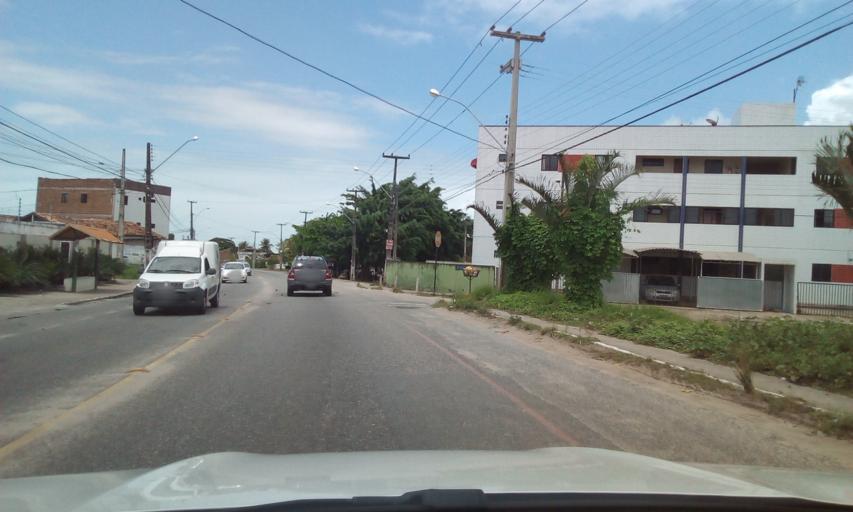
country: BR
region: Paraiba
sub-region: Joao Pessoa
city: Joao Pessoa
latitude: -7.1823
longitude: -34.8596
